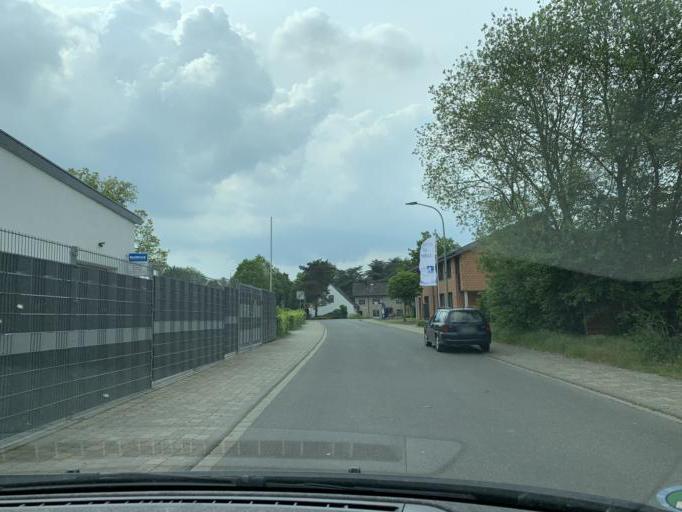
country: DE
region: North Rhine-Westphalia
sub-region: Regierungsbezirk Koln
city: Vettweiss
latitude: 50.7427
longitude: 6.6039
